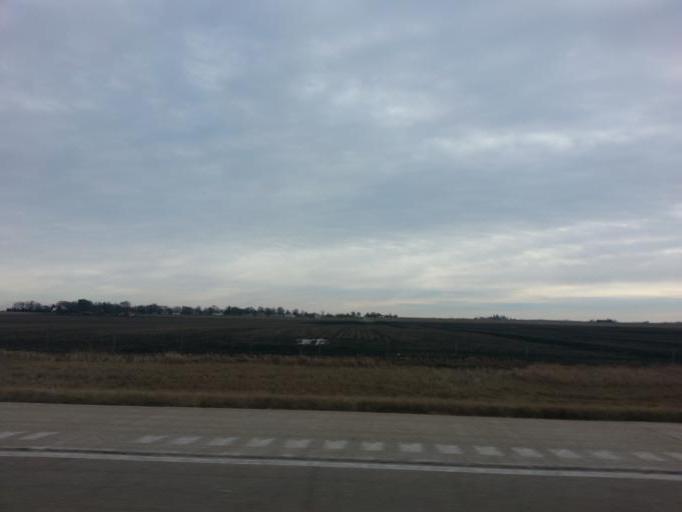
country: US
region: Illinois
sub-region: Woodford County
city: El Paso
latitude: 40.7802
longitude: -89.0348
